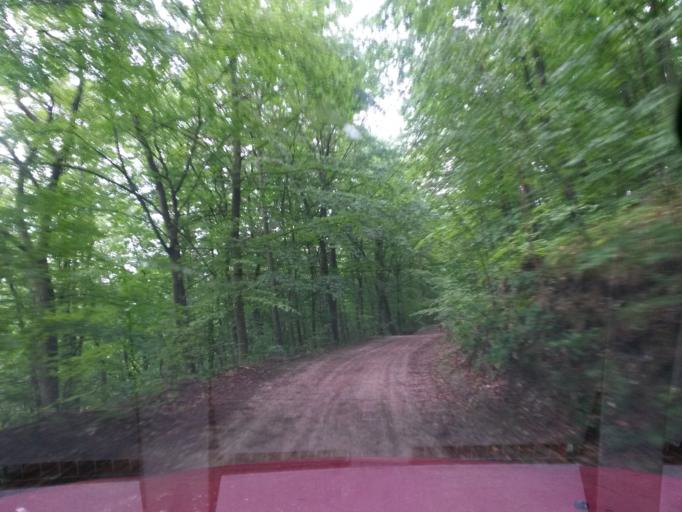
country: SK
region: Kosicky
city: Kosice
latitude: 48.7229
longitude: 21.1669
